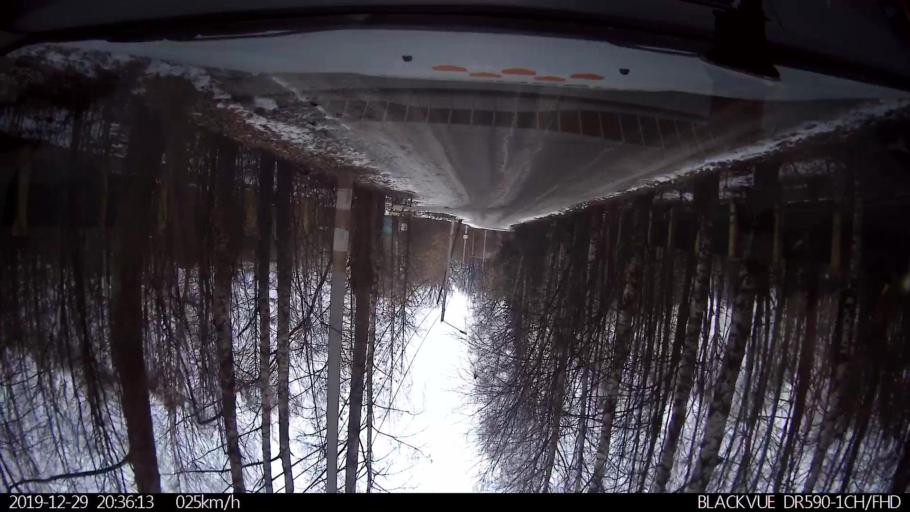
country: RU
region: Nizjnij Novgorod
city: Afonino
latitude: 56.1917
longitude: 44.0472
